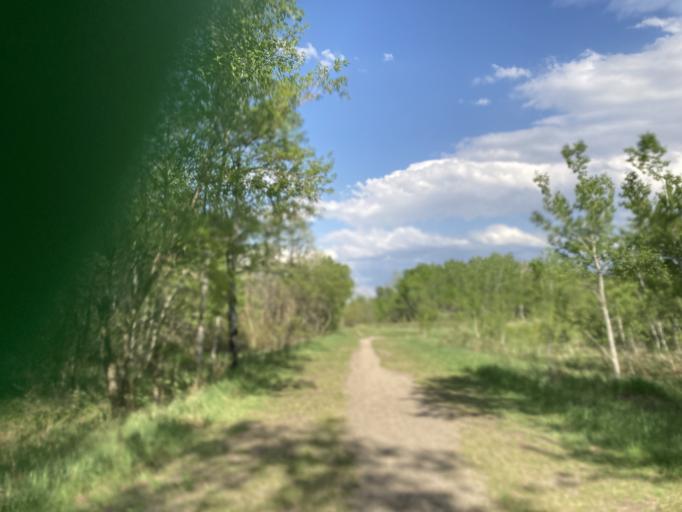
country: CA
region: Manitoba
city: Brandon
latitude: 49.7239
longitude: -99.9098
